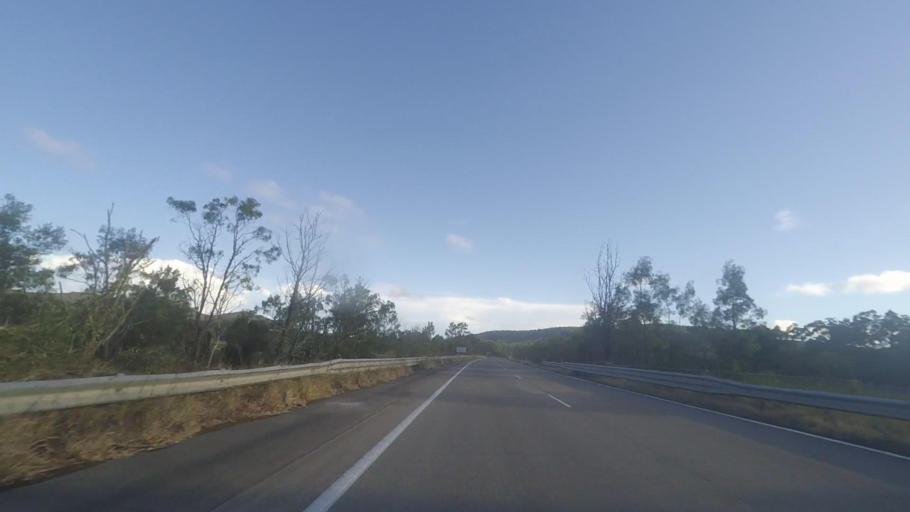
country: AU
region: New South Wales
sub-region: Great Lakes
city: Nabiac
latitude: -32.2619
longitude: 152.3274
